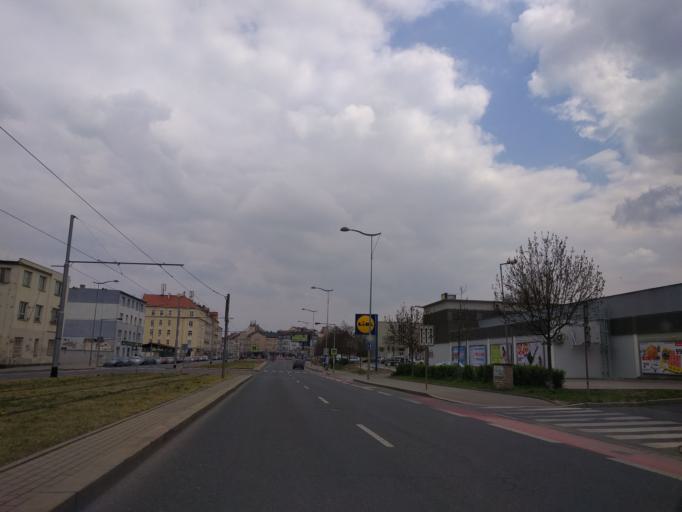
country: CZ
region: Praha
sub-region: Praha 9
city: Prosek
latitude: 50.1023
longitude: 14.4989
